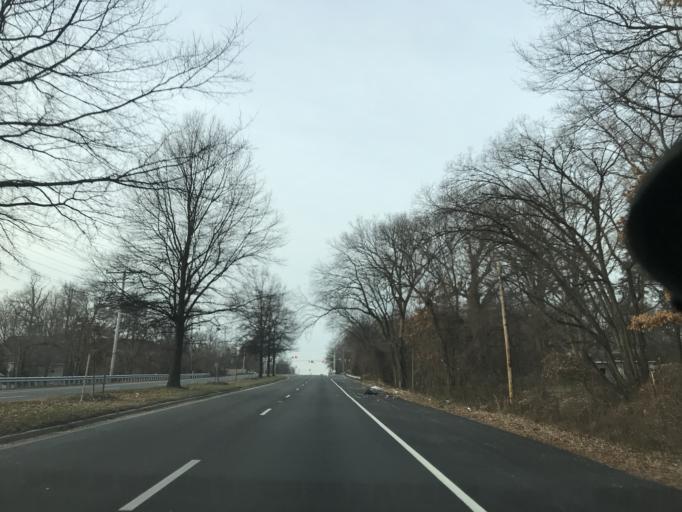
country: US
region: Maryland
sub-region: Prince George's County
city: Springdale
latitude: 38.9423
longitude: -76.8517
